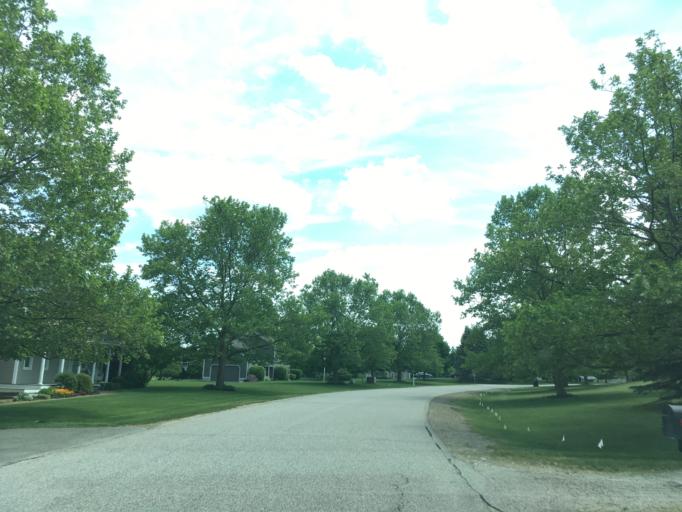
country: US
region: New Hampshire
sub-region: Rockingham County
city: Stratham Station
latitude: 43.0270
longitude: -70.8759
